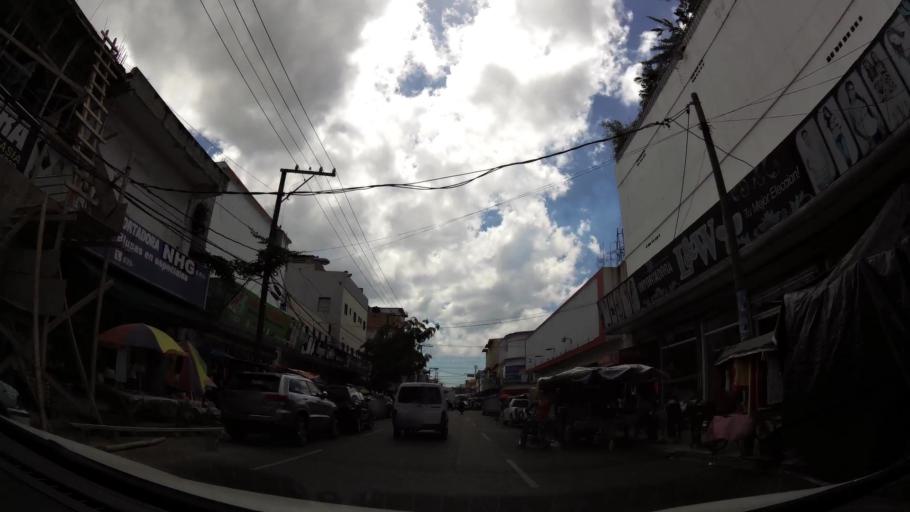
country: DO
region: Nacional
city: San Carlos
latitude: 18.4860
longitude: -69.8938
